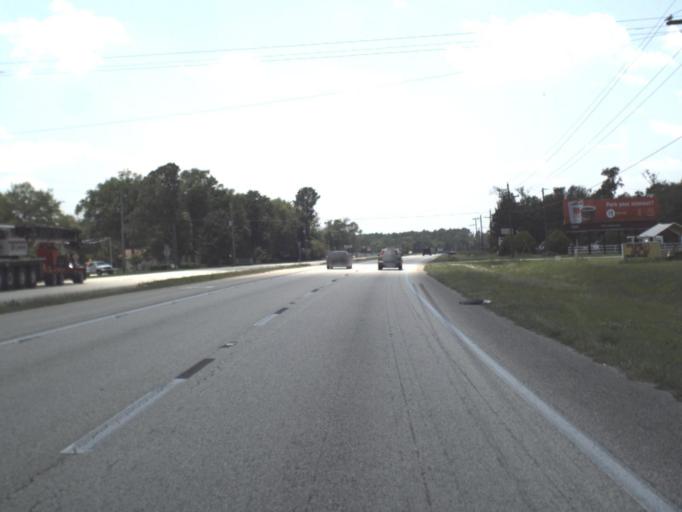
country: US
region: Florida
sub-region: Bradford County
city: Starke
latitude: 29.8884
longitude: -82.1421
